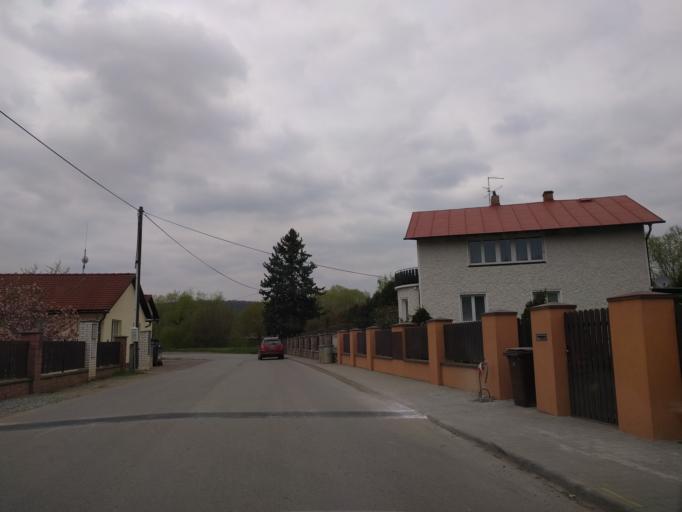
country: CZ
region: Central Bohemia
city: Revnice
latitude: 49.9175
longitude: 14.2490
